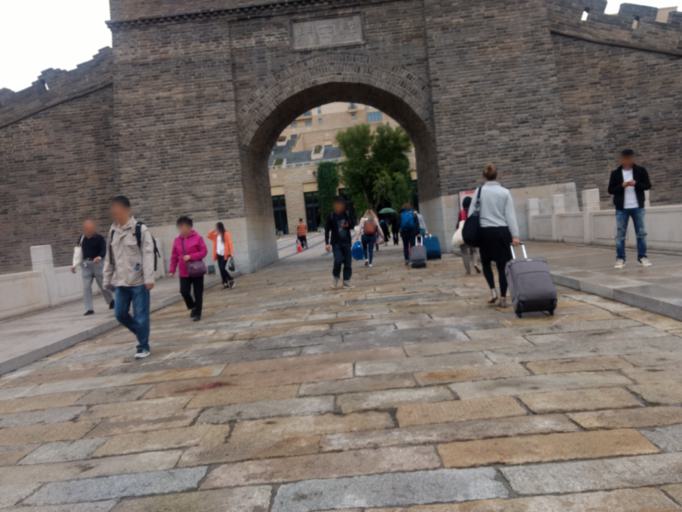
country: CN
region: Beijing
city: Xinchengzi
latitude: 40.6438
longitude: 117.2624
